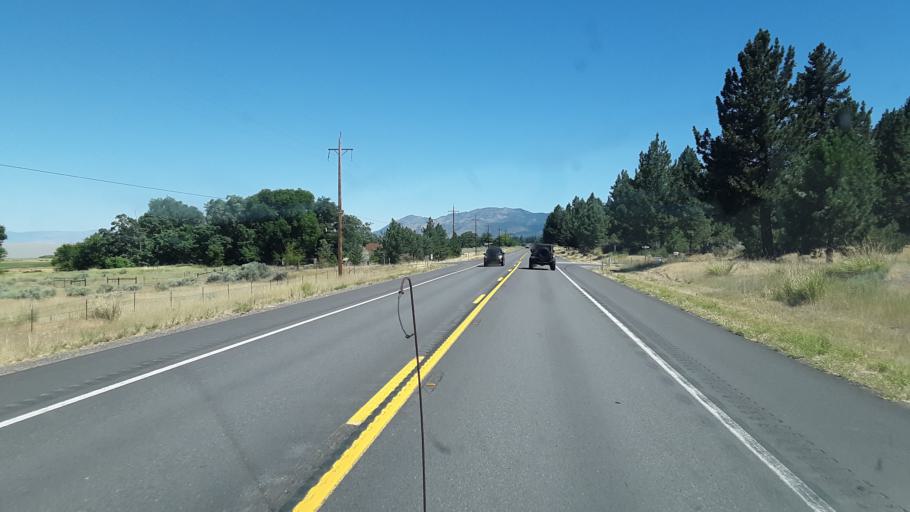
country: US
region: California
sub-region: Lassen County
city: Janesville
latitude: 40.2423
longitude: -120.4550
